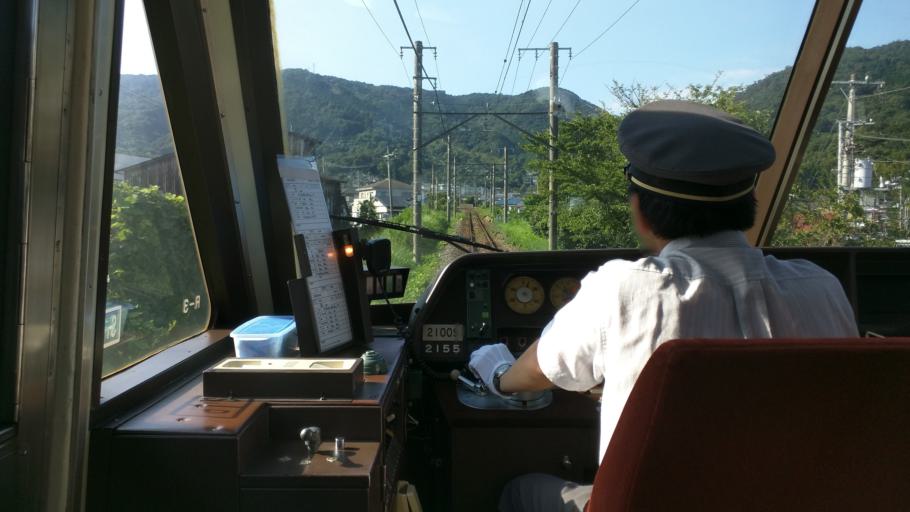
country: JP
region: Shizuoka
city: Ito
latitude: 35.0083
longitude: 139.0791
